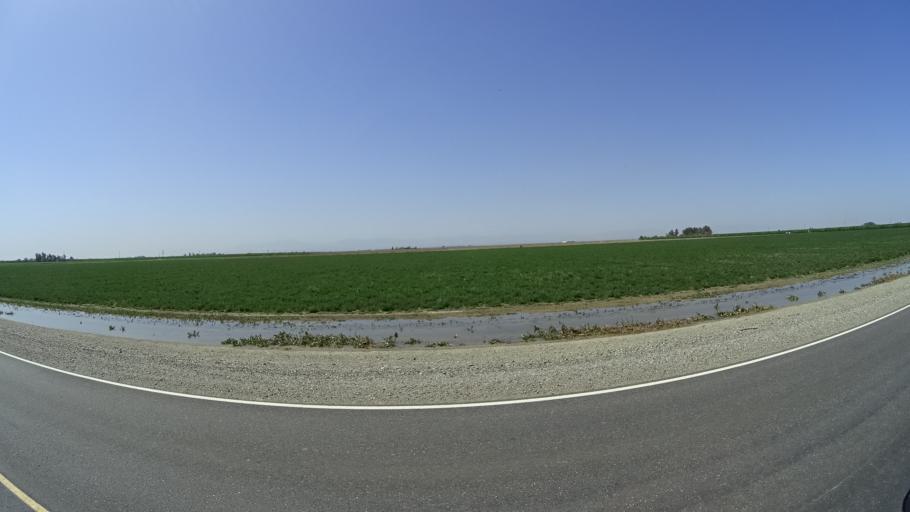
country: US
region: California
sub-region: Glenn County
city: Willows
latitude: 39.5925
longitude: -122.1371
